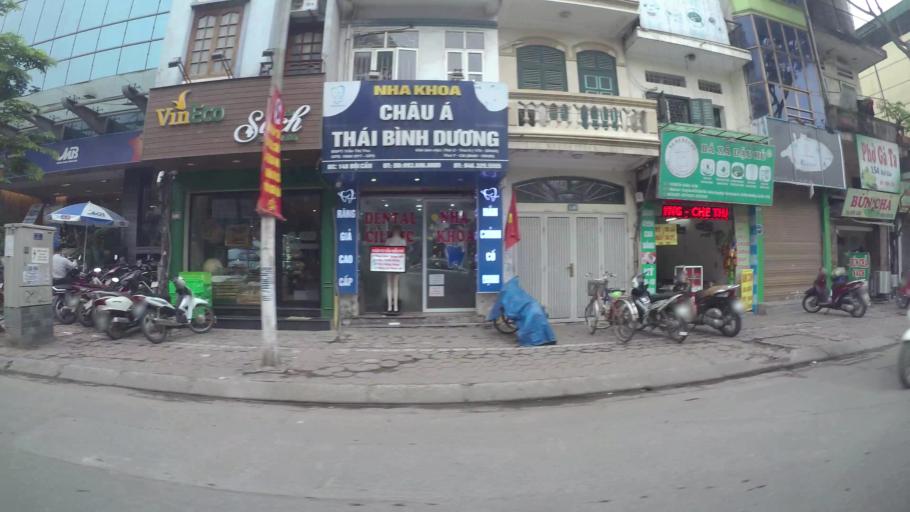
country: VN
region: Ha Noi
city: Dong Da
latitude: 21.0346
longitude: 105.8261
